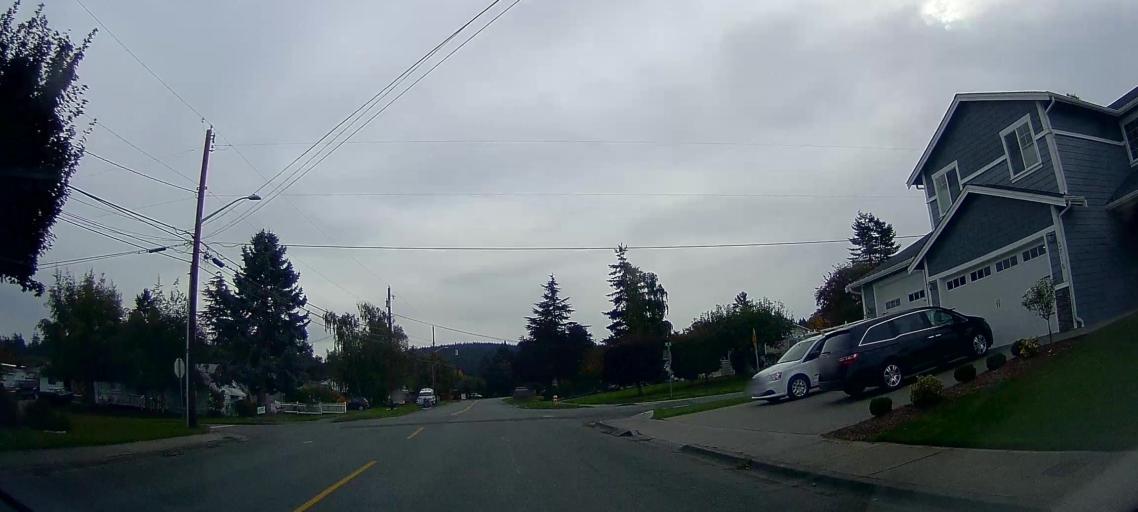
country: US
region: Washington
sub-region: Skagit County
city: Anacortes
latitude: 48.4919
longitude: -122.6176
